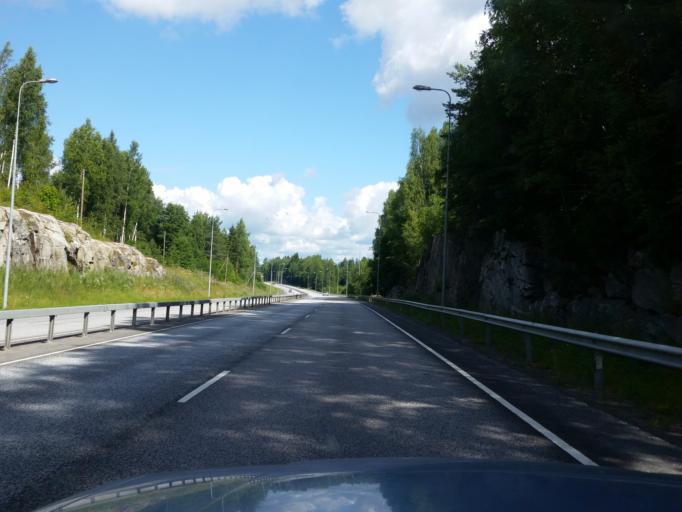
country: FI
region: Uusimaa
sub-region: Helsinki
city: Vihti
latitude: 60.3162
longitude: 24.3465
